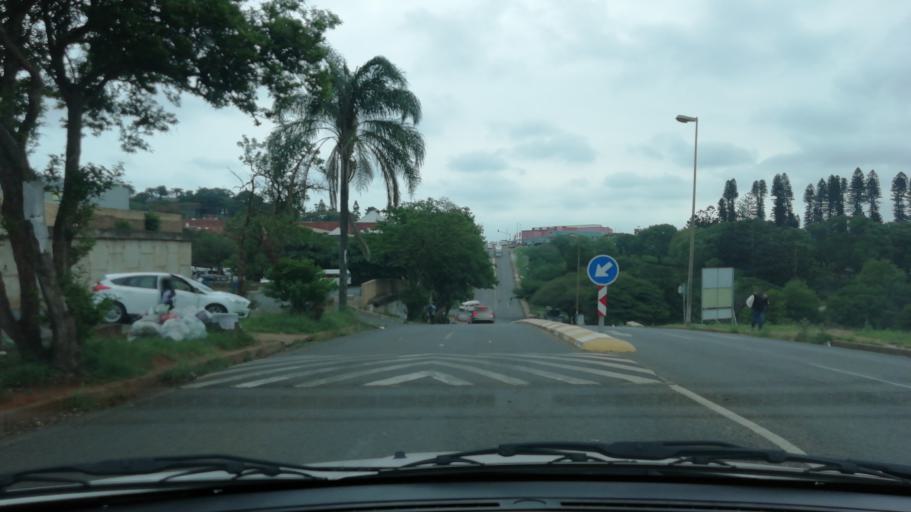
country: ZA
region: KwaZulu-Natal
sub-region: uThungulu District Municipality
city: Empangeni
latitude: -28.7423
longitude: 31.8875
